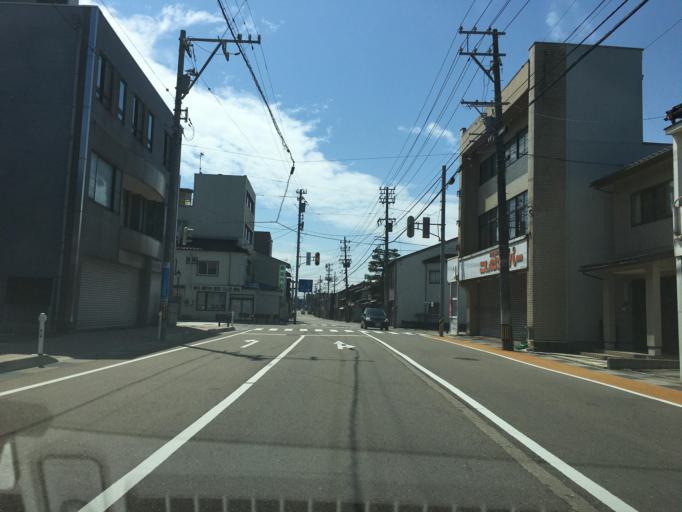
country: JP
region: Toyama
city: Himi
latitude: 36.8503
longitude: 136.9878
